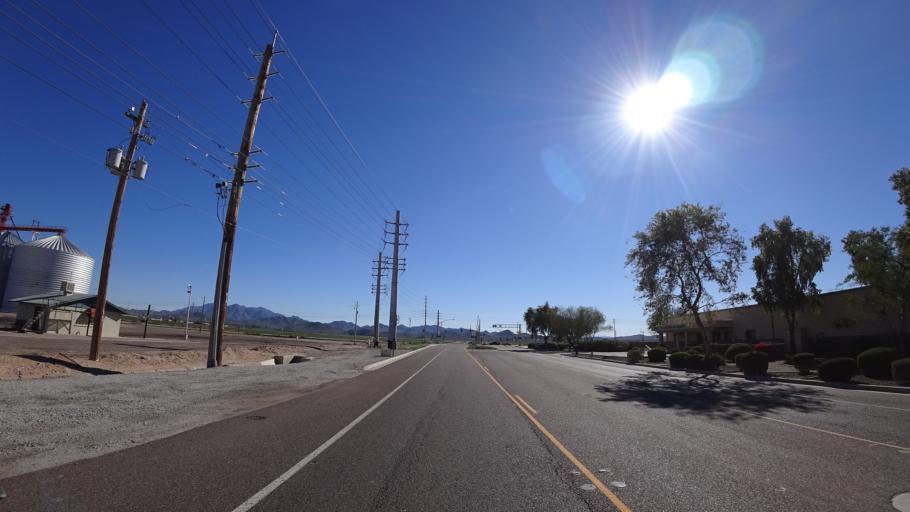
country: US
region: Arizona
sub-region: Maricopa County
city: Goodyear
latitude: 33.4081
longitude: -112.4093
